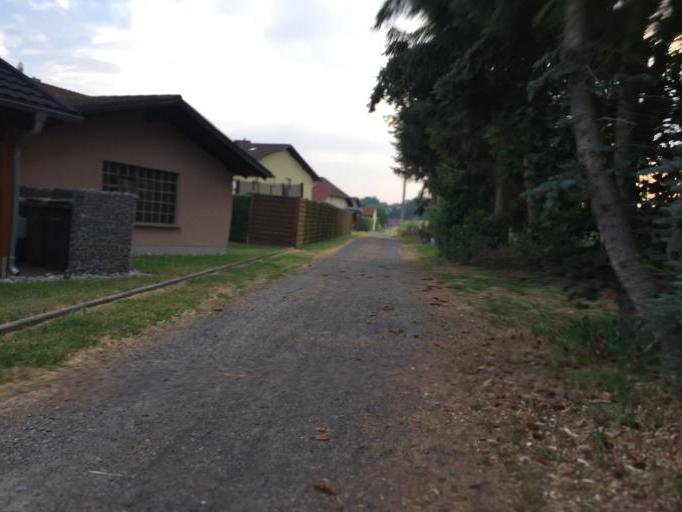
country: DE
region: Rheinland-Pfalz
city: Weroth
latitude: 50.4630
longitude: 7.9503
